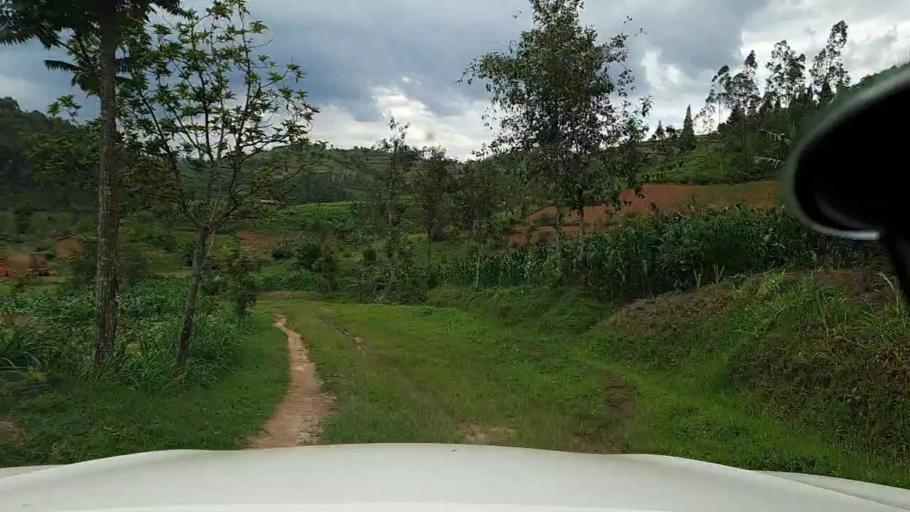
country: RW
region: Southern Province
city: Gitarama
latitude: -1.8140
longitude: 29.7998
